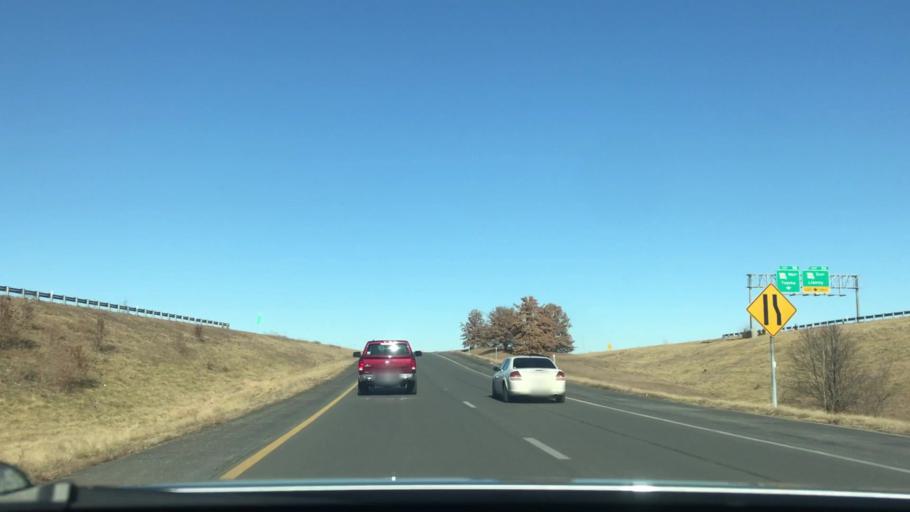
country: US
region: Missouri
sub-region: Platte County
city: Weatherby Lake
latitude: 39.2475
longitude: -94.6578
